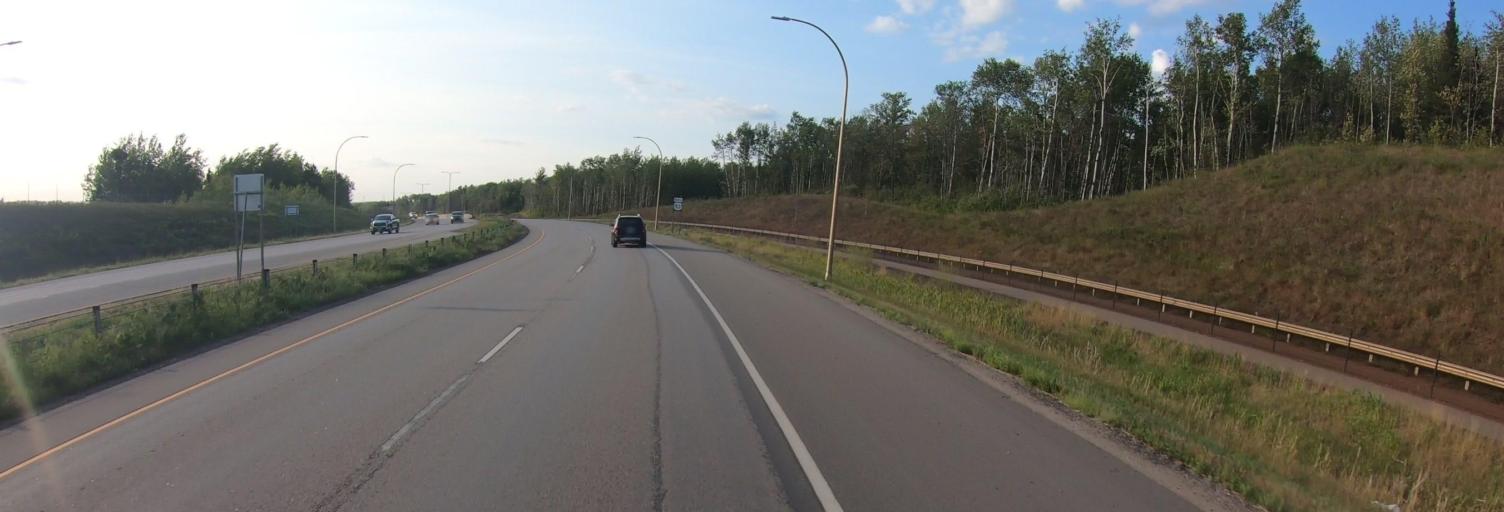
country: US
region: Minnesota
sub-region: Saint Louis County
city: Virginia
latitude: 47.5126
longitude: -92.5118
